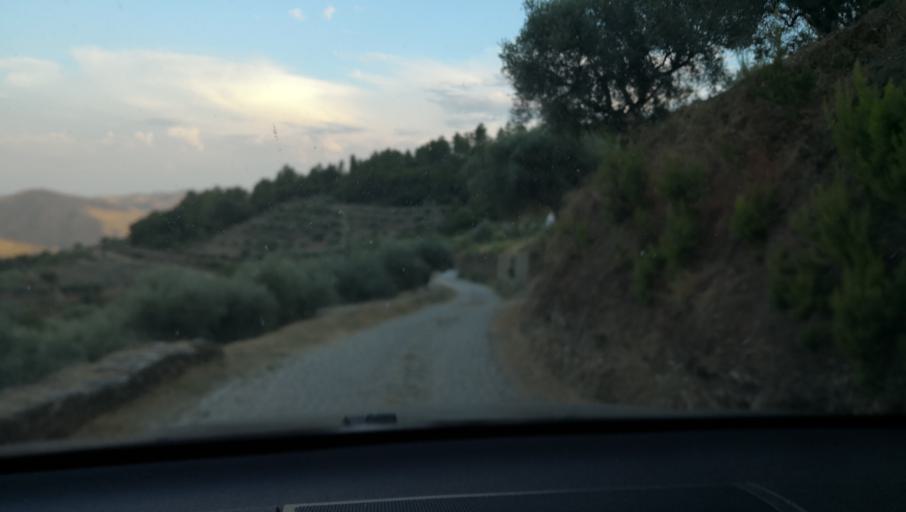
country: PT
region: Vila Real
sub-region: Sabrosa
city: Vilela
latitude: 41.1950
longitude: -7.5700
